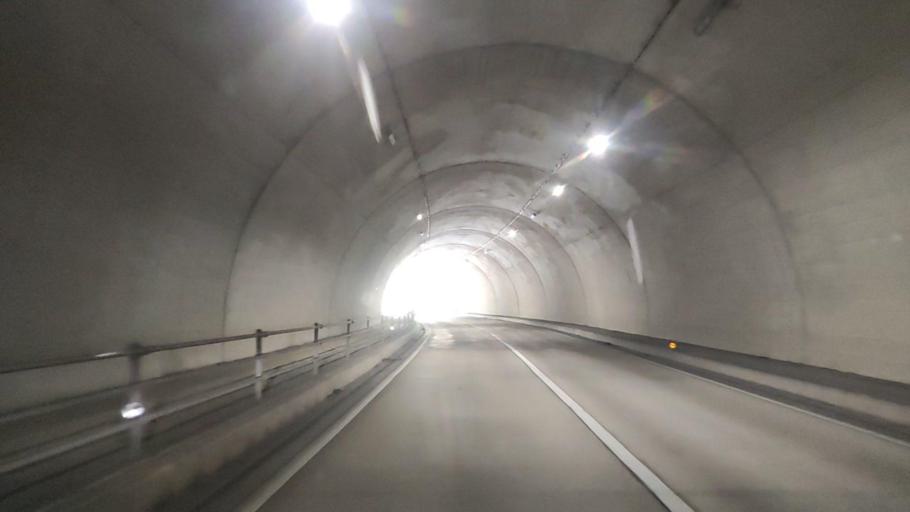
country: JP
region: Gifu
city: Godo
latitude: 35.5590
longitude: 136.6410
